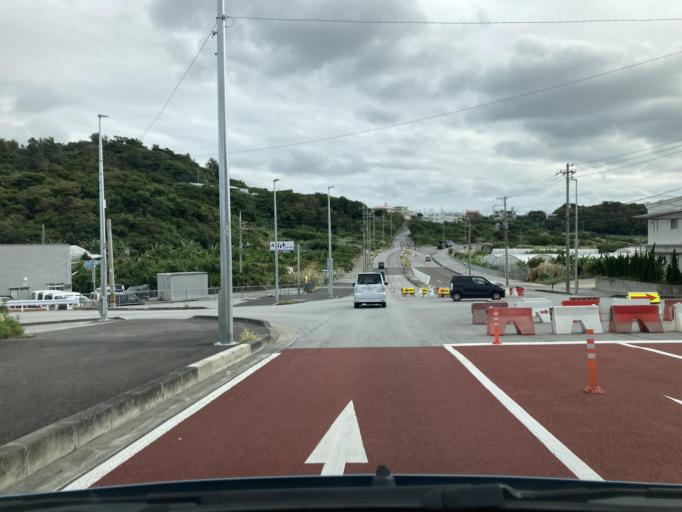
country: JP
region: Okinawa
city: Tomigusuku
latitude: 26.1663
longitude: 127.6781
